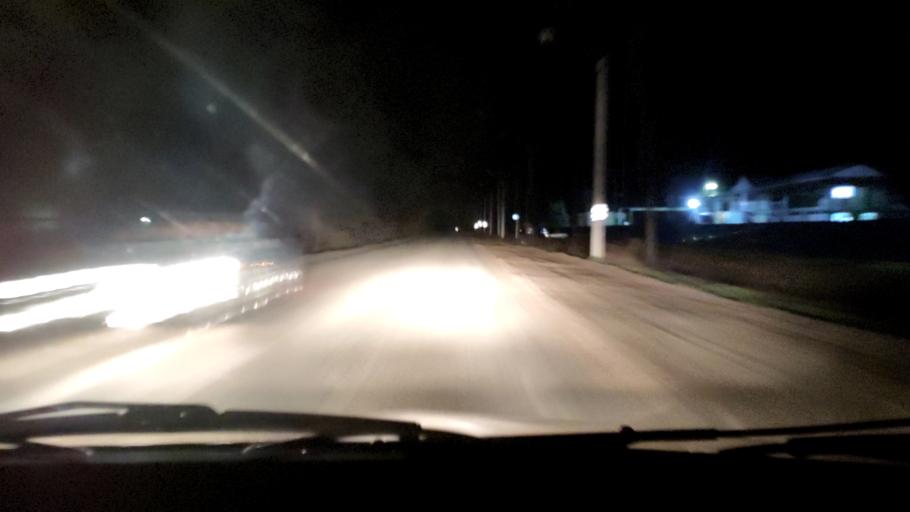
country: RU
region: Voronezj
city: Podkletnoye
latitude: 51.6427
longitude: 39.4872
